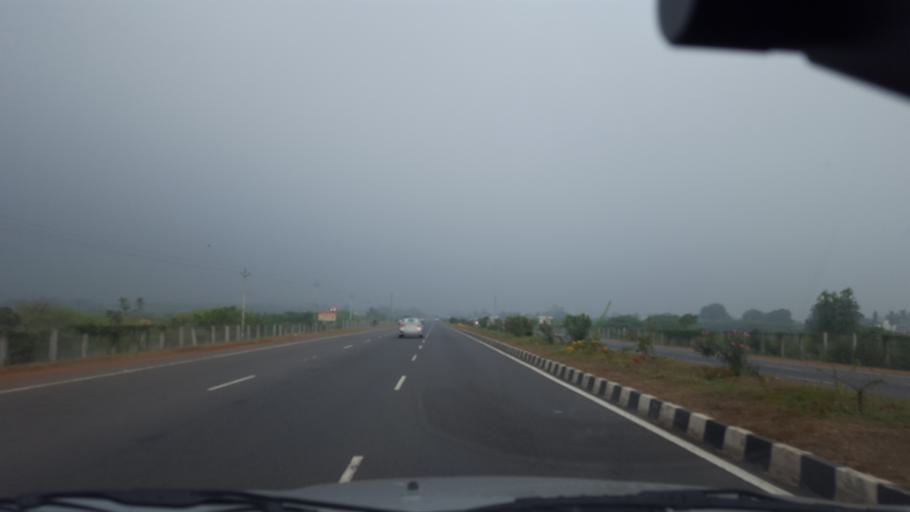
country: IN
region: Andhra Pradesh
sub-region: Prakasam
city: Ongole
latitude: 15.5792
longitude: 80.0414
